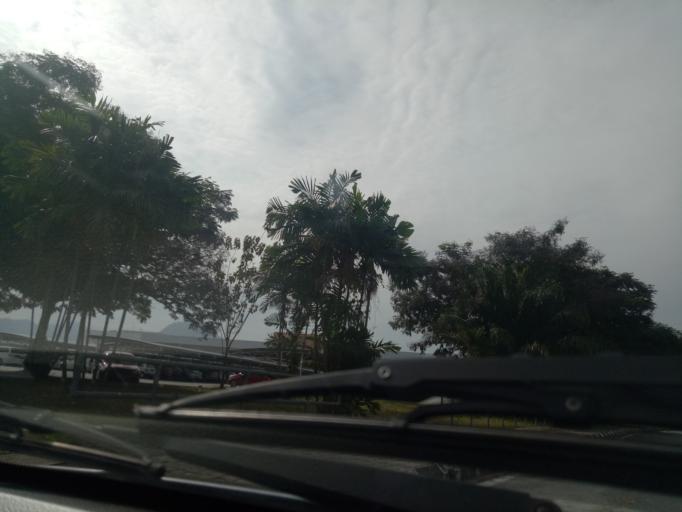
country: MY
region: Perak
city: Ipoh
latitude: 4.6172
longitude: 101.1170
